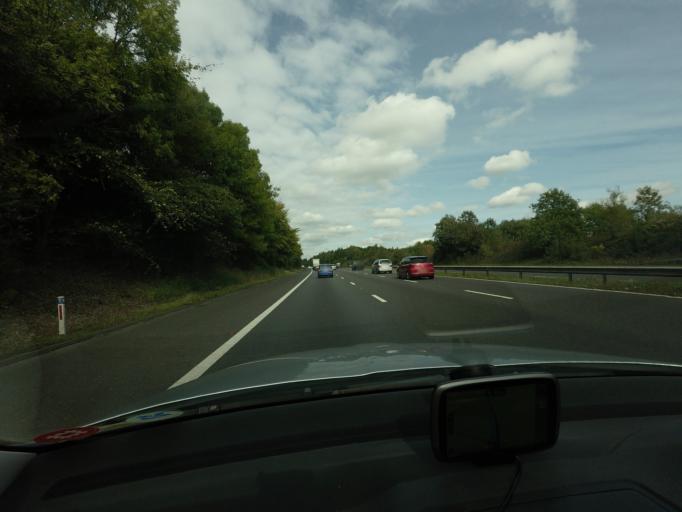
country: GB
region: England
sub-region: Kent
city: Shoreham
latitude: 51.3287
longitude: 0.1592
